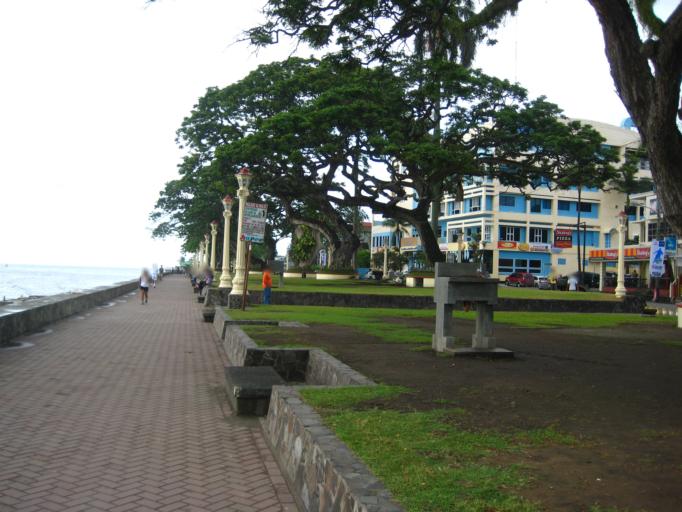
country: PH
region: Central Visayas
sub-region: Province of Negros Oriental
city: Dumaguete
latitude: 9.3073
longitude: 123.3101
